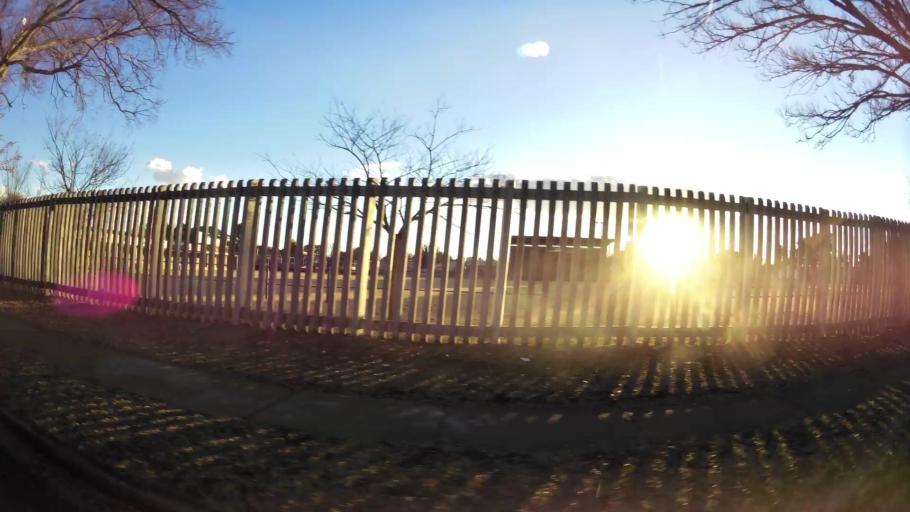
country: ZA
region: North-West
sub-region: Dr Kenneth Kaunda District Municipality
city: Potchefstroom
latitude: -26.7263
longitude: 27.0920
